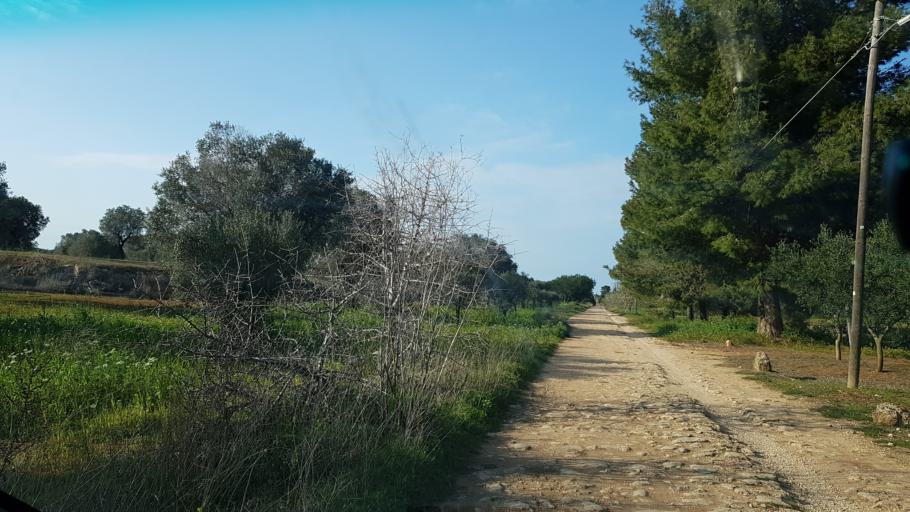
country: IT
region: Apulia
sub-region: Provincia di Brindisi
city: San Vito dei Normanni
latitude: 40.6742
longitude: 17.7903
